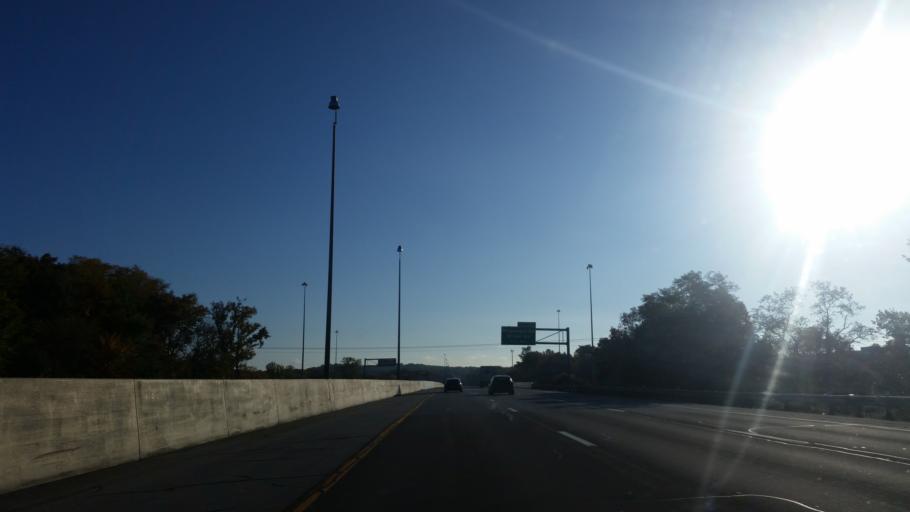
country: US
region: Ohio
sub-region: Summit County
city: Fairlawn
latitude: 41.1191
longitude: -81.6414
